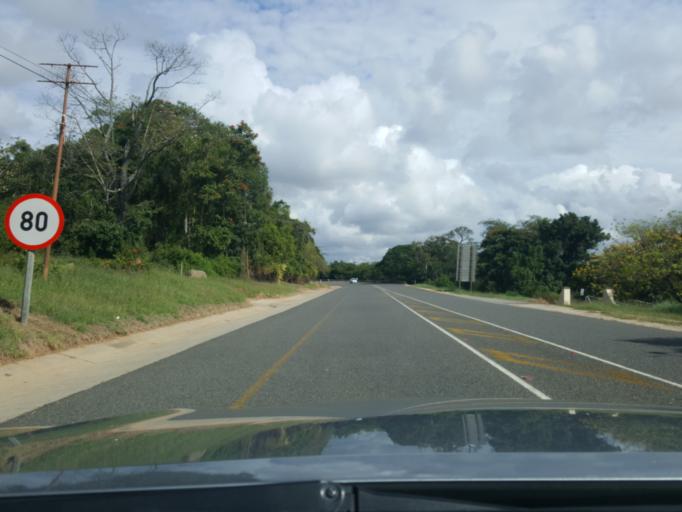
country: ZA
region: Mpumalanga
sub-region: Ehlanzeni District
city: Nelspruit
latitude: -25.4679
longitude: 31.0422
